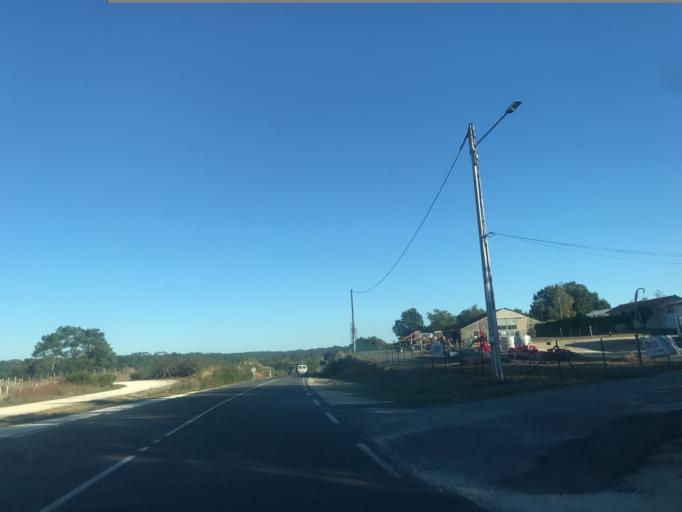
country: FR
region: Poitou-Charentes
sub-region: Departement de la Charente-Maritime
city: Montguyon
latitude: 45.2089
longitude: -0.1654
